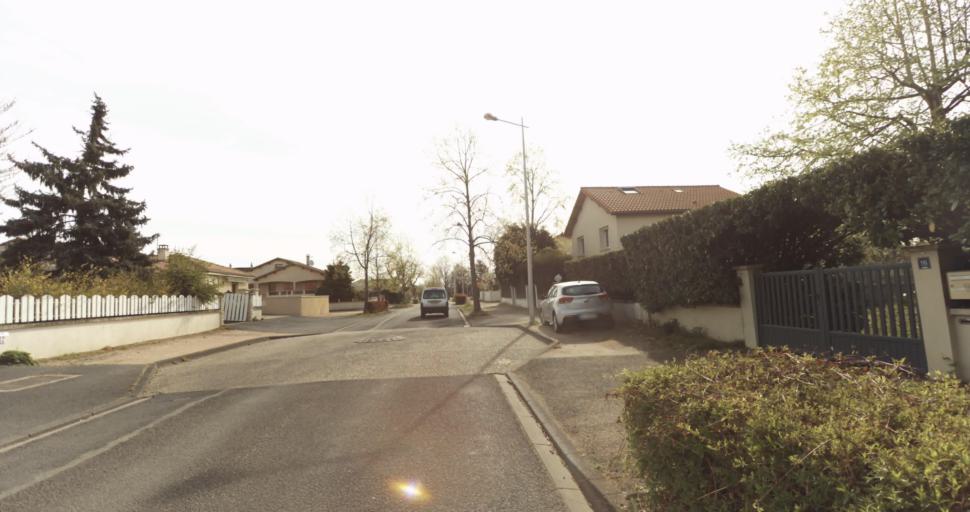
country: FR
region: Auvergne
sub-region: Departement du Puy-de-Dome
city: Cebazat
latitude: 45.8317
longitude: 3.1073
